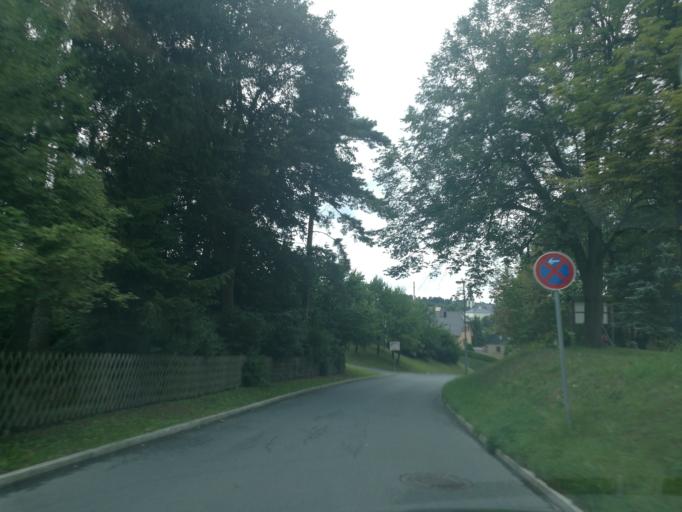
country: DE
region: Saxony
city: Adorf
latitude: 50.3161
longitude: 12.2627
